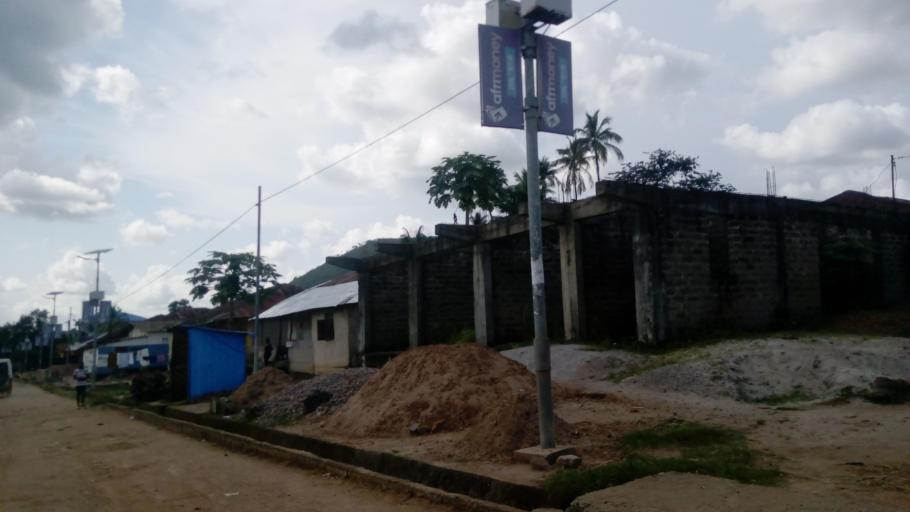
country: SL
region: Northern Province
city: Makeni
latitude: 8.8914
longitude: -12.0458
